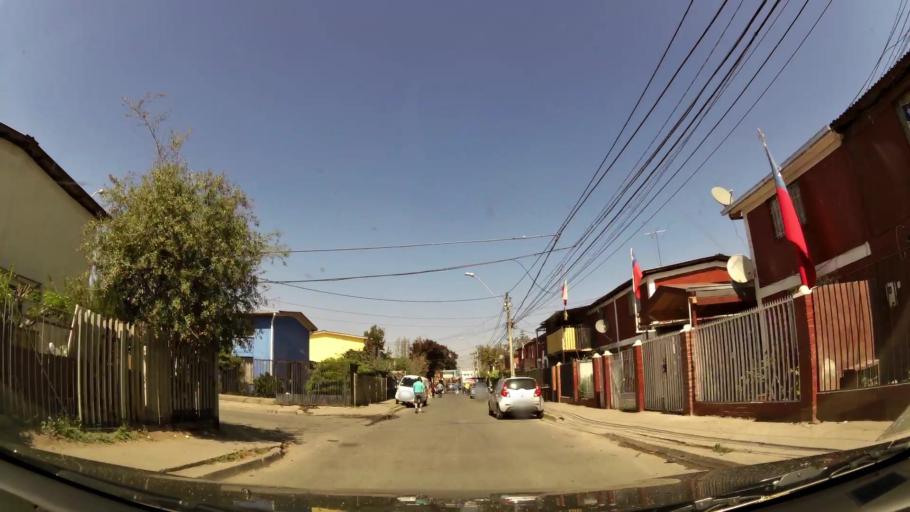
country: CL
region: Santiago Metropolitan
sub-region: Provincia de Santiago
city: Lo Prado
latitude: -33.3633
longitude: -70.7468
